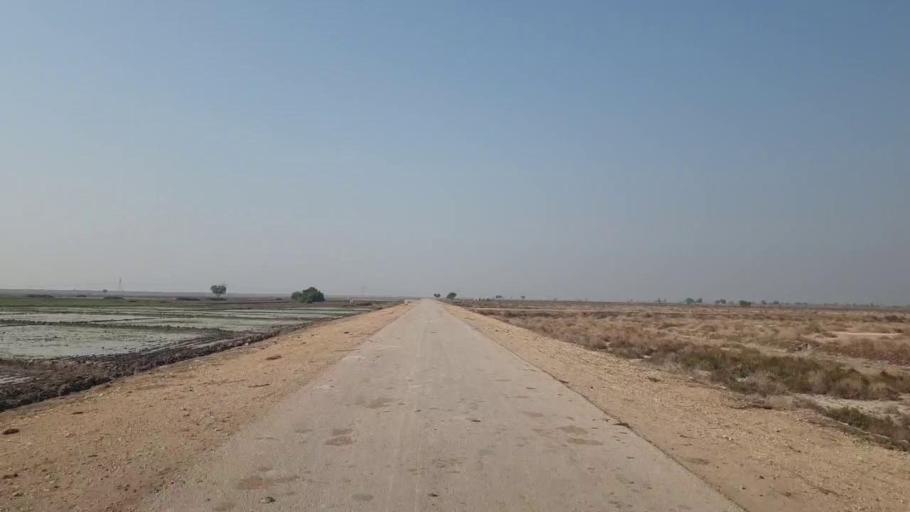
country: PK
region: Sindh
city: Sehwan
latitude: 26.4179
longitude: 67.8119
